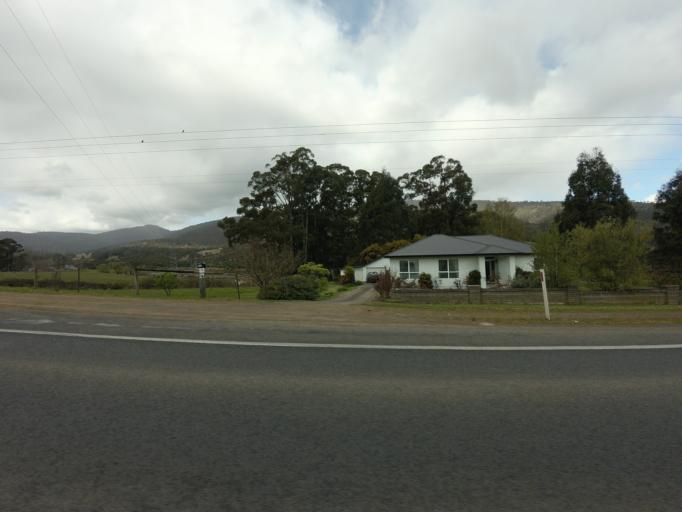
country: AU
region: Tasmania
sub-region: Huon Valley
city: Huonville
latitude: -43.0415
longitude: 147.0447
